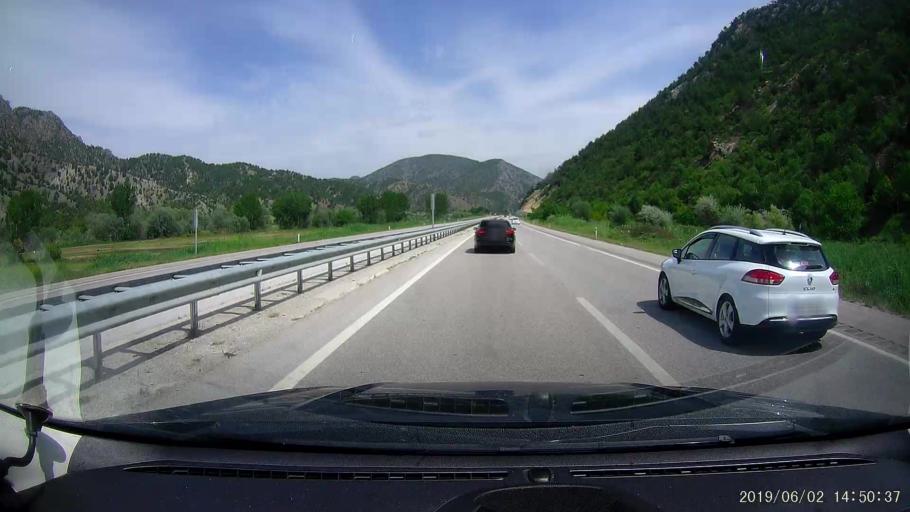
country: TR
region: Corum
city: Kargi
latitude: 41.0705
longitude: 34.5237
